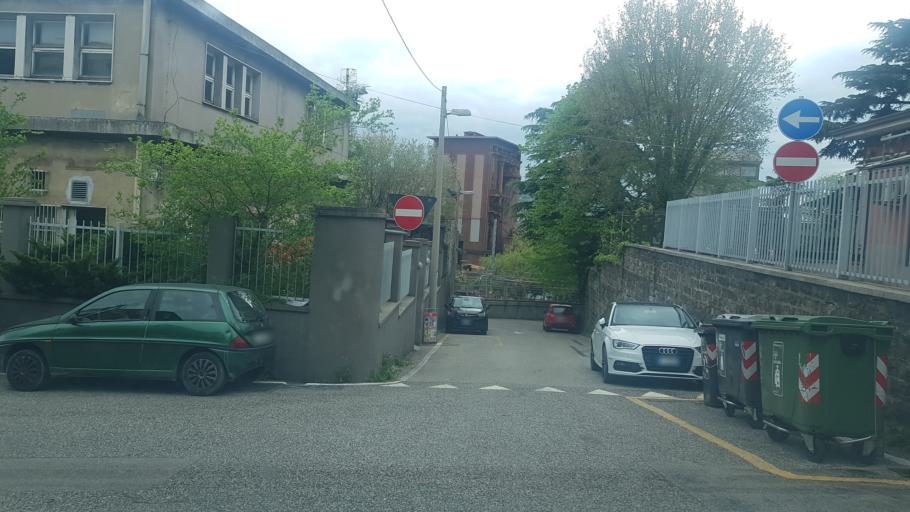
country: IT
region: Friuli Venezia Giulia
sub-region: Provincia di Trieste
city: Trieste
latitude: 45.6235
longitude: 13.7797
